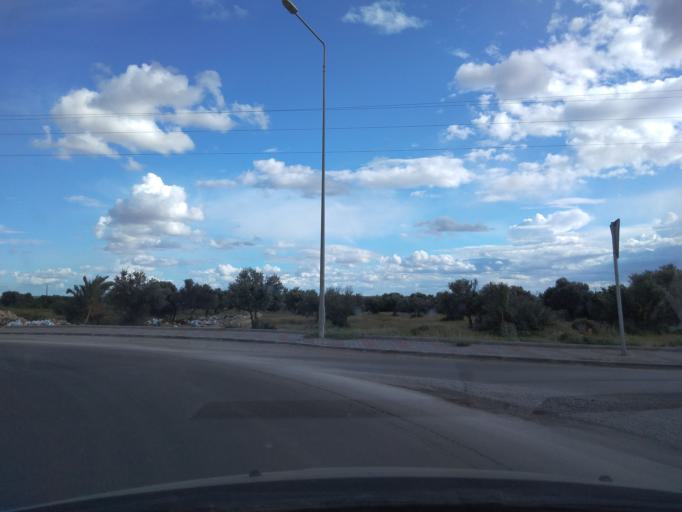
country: TN
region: Susah
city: Masakin
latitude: 35.7106
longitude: 10.5565
